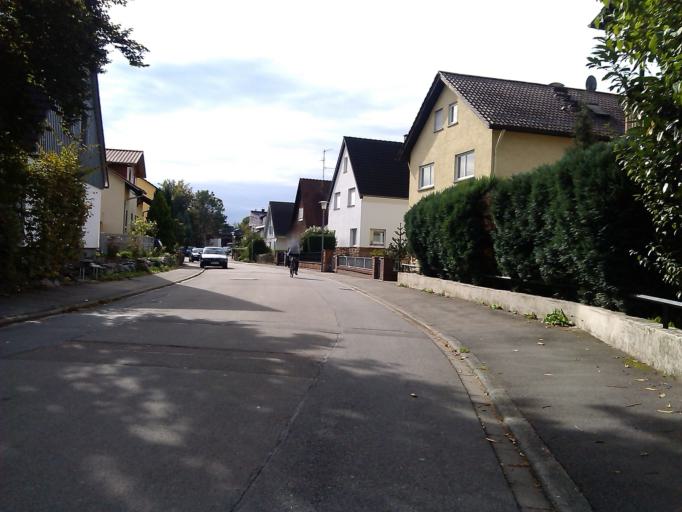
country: DE
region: Baden-Wuerttemberg
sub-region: Karlsruhe Region
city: Hemsbach
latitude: 49.5937
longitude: 8.6503
